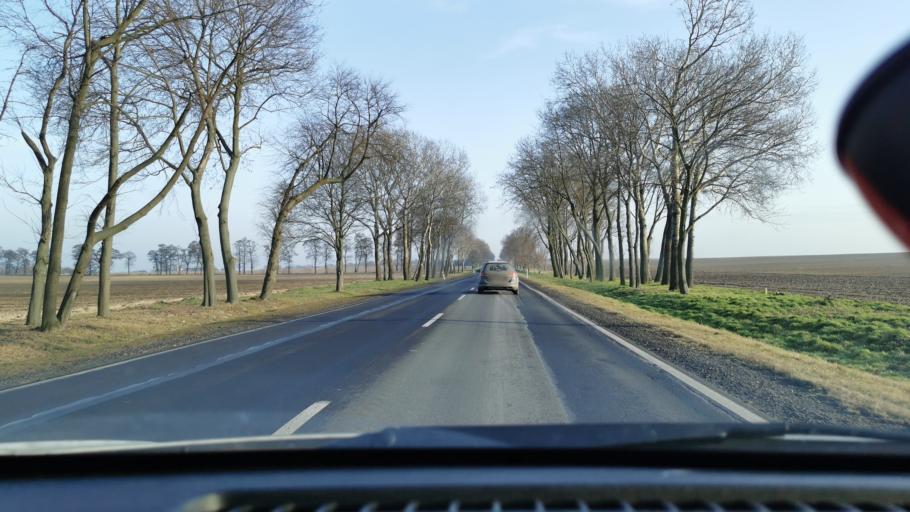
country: PL
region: Lodz Voivodeship
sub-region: Powiat sieradzki
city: Wroblew
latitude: 51.6214
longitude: 18.5823
